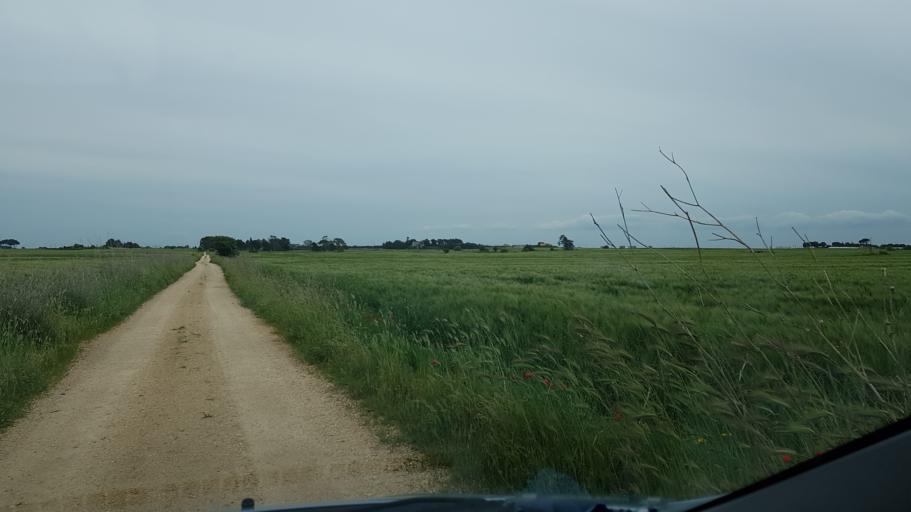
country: IT
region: Apulia
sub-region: Provincia di Brindisi
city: Brindisi
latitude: 40.6564
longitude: 17.8814
